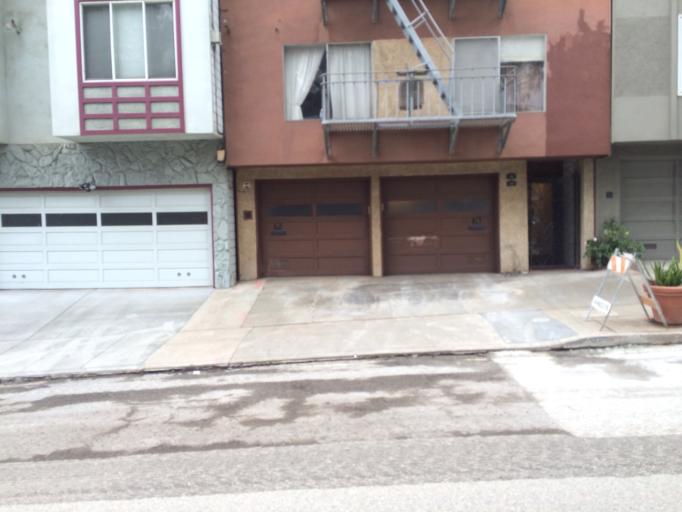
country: US
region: California
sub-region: San Francisco County
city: San Francisco
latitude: 37.7647
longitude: -122.4403
